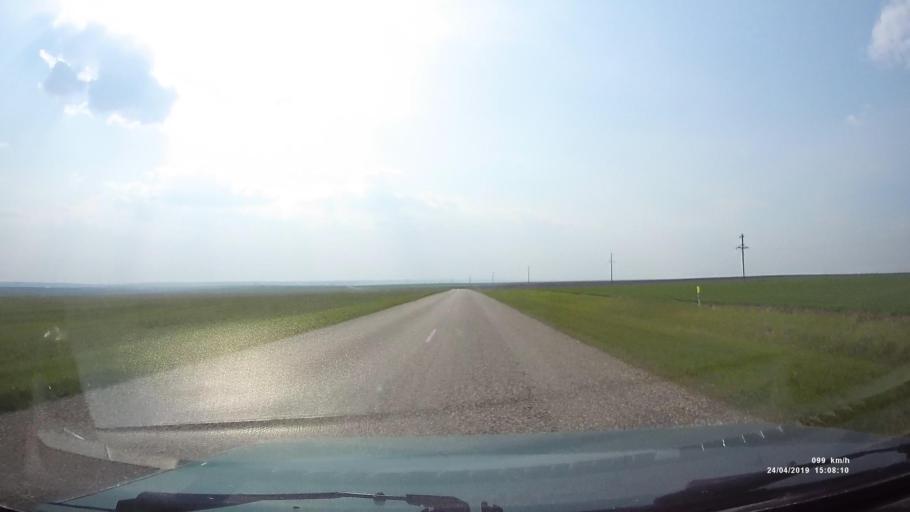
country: RU
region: Rostov
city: Remontnoye
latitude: 46.5600
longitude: 43.3890
